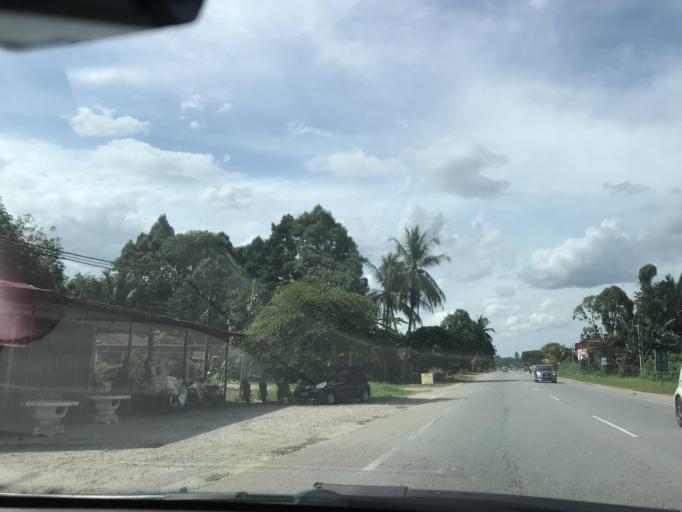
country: MY
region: Kelantan
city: Tanah Merah
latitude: 5.8509
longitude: 102.1646
